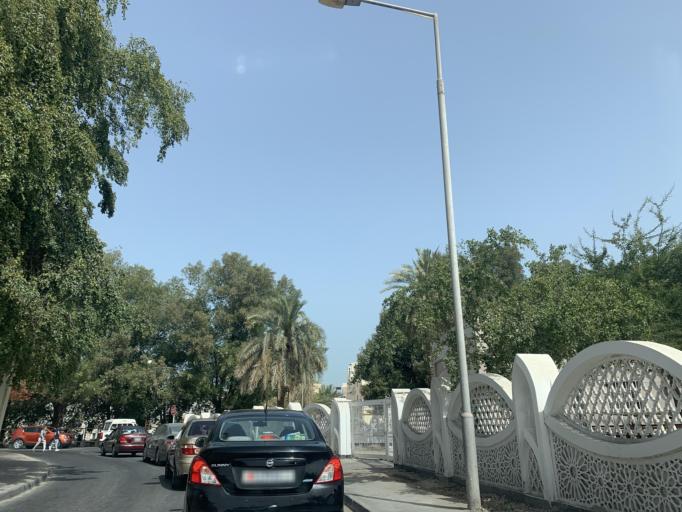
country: BH
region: Manama
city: Manama
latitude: 26.2254
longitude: 50.5679
